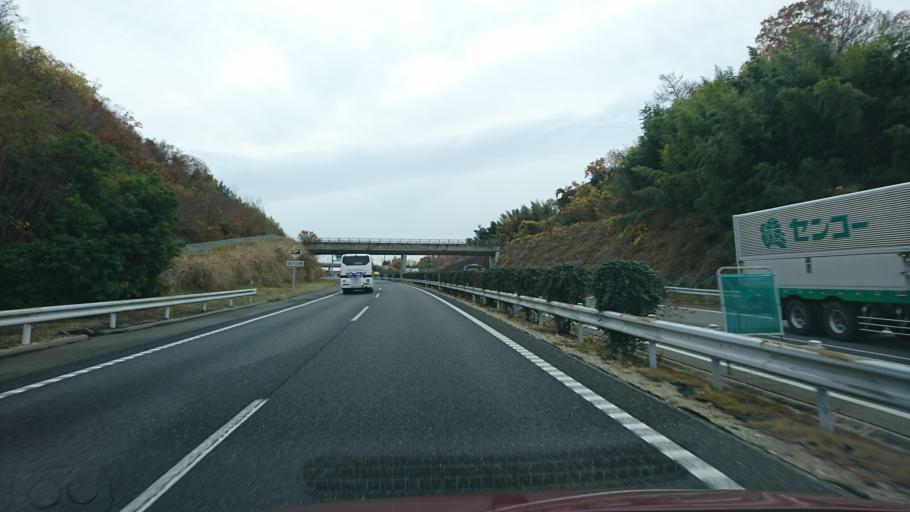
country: JP
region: Hyogo
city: Sandacho
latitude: 34.8208
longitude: 135.1356
